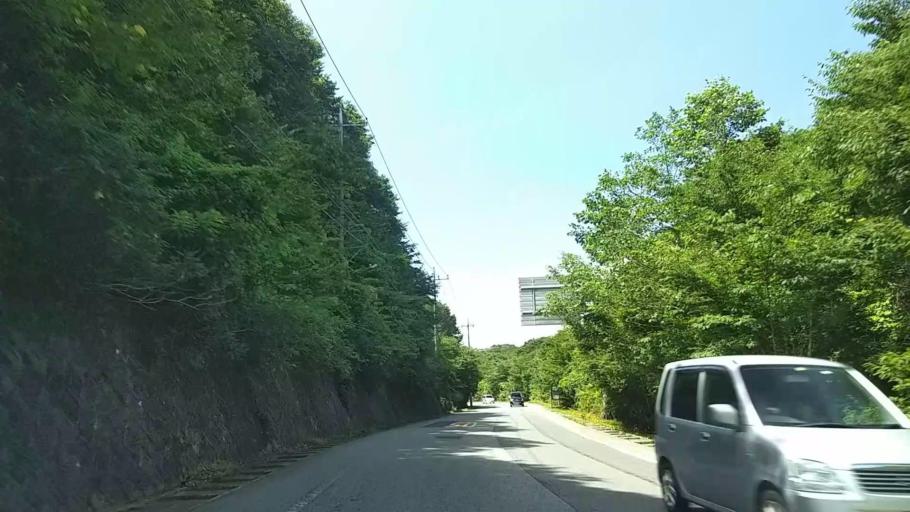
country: JP
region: Shizuoka
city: Gotemba
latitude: 35.2581
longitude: 138.8099
